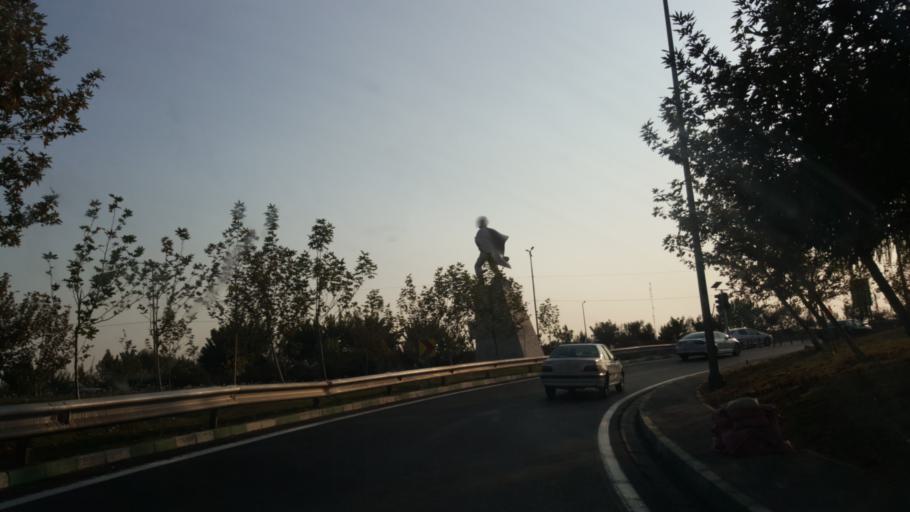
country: IR
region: Tehran
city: Tehran
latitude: 35.7541
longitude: 51.2963
